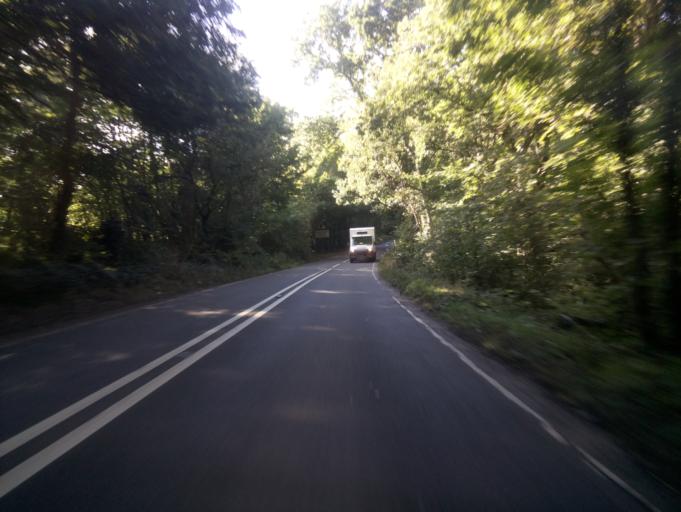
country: GB
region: England
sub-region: Devon
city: Newton Poppleford
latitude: 50.7037
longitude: -3.3461
